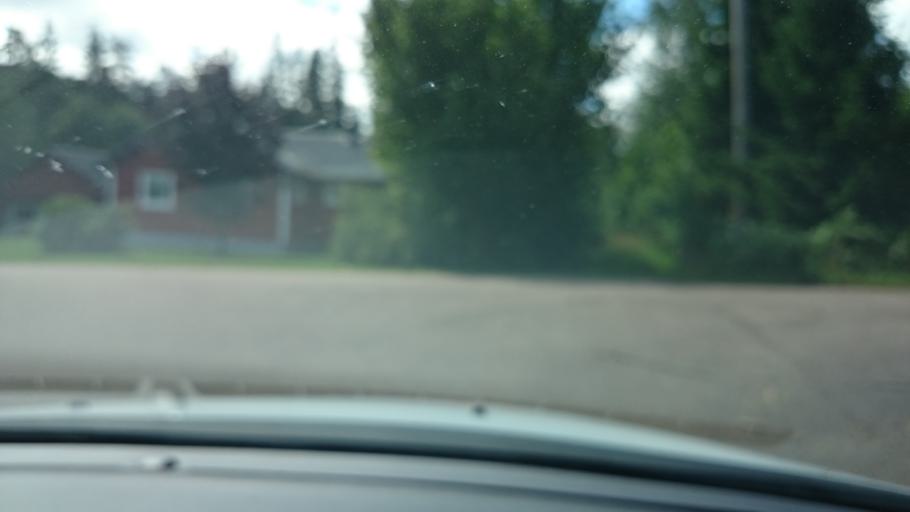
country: SE
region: Halland
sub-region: Hylte Kommun
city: Torup
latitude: 56.9569
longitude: 13.0913
